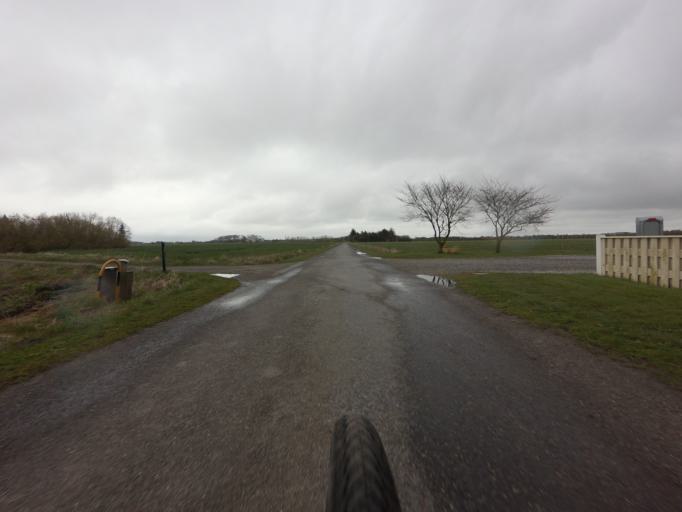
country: DK
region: North Denmark
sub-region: Bronderslev Kommune
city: Bronderslev
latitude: 57.3218
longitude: 9.8091
